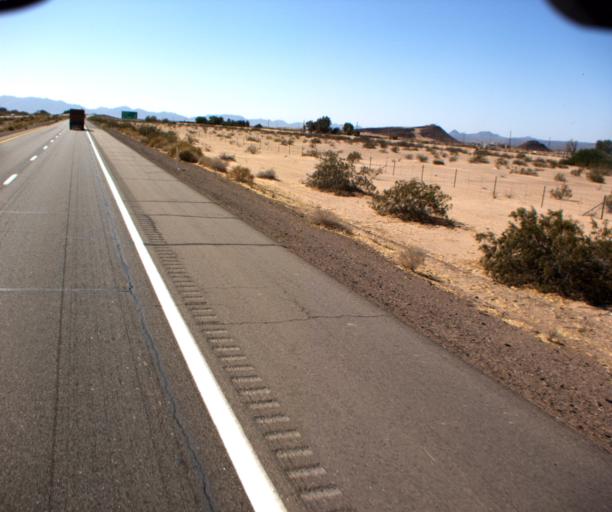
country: US
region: Arizona
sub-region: Yuma County
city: Wellton
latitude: 32.6790
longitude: -114.0350
